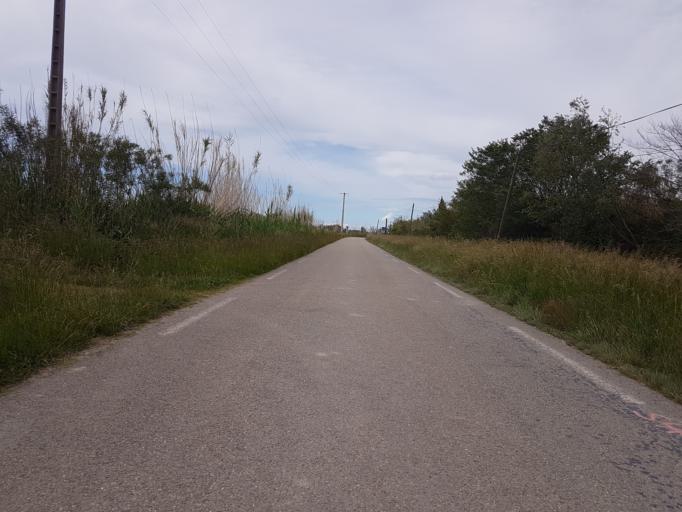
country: FR
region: Languedoc-Roussillon
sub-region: Departement du Gard
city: Saint-Gilles
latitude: 43.6061
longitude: 4.3842
